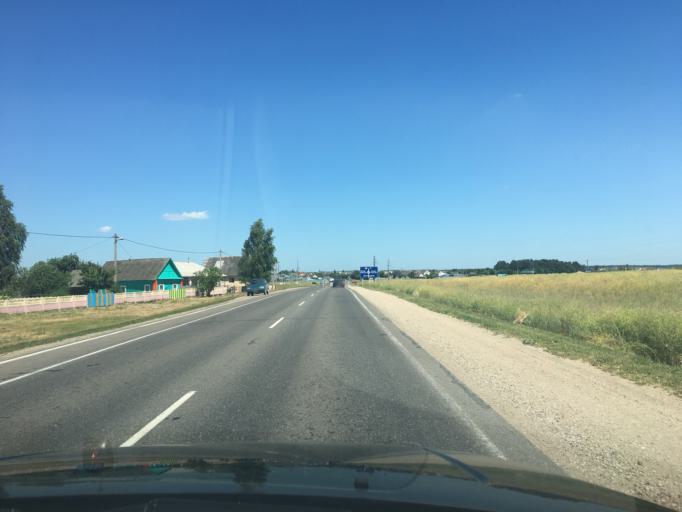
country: BY
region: Grodnenskaya
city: Iwye
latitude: 53.9116
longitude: 25.7630
